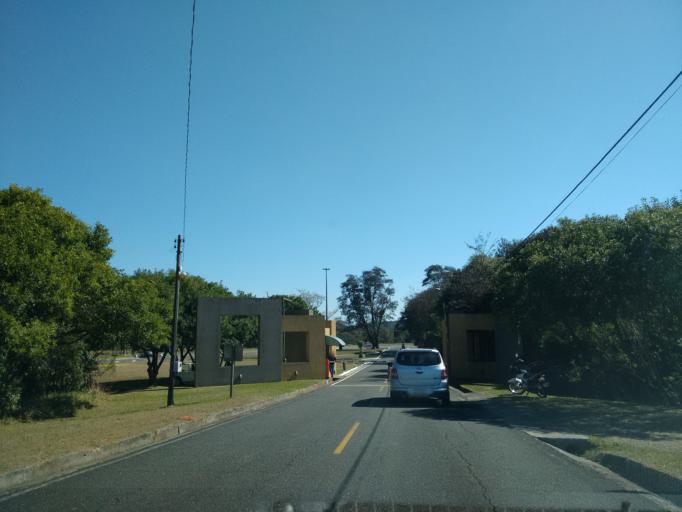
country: BR
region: Parana
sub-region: Palmeira
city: Palmeira
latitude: -25.2464
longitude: -50.0210
